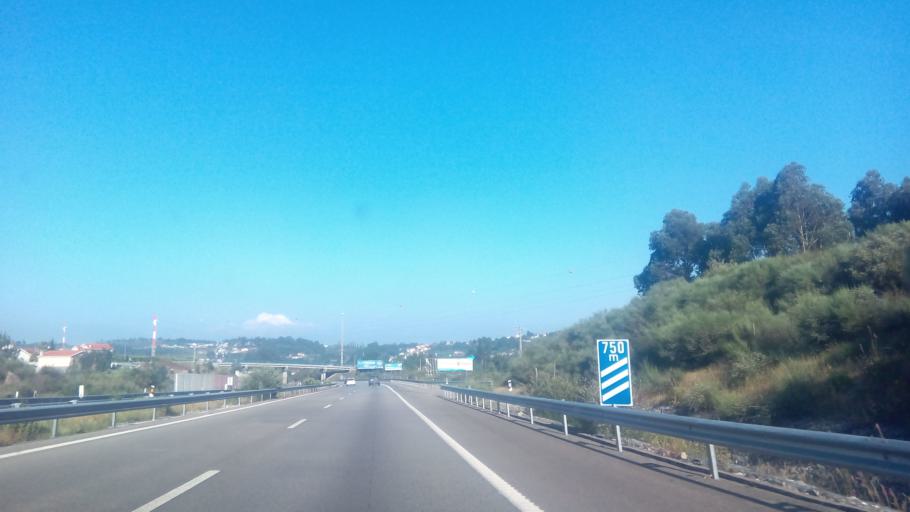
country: PT
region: Porto
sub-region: Pacos de Ferreira
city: Frazao
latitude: 41.2549
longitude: -8.4132
